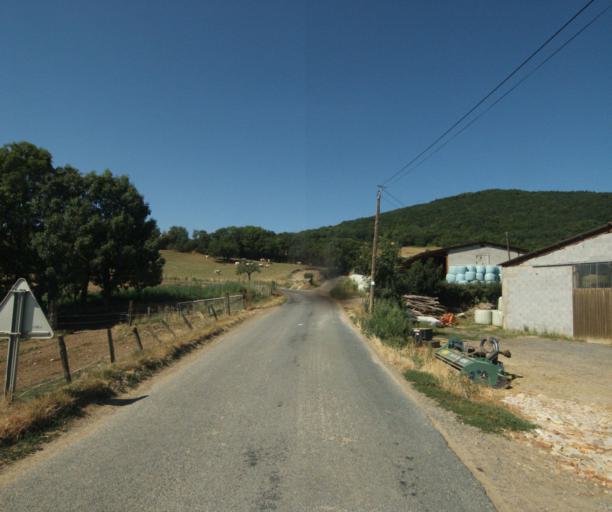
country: FR
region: Rhone-Alpes
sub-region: Departement du Rhone
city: Saint-Romain-de-Popey
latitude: 45.8232
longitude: 4.5334
